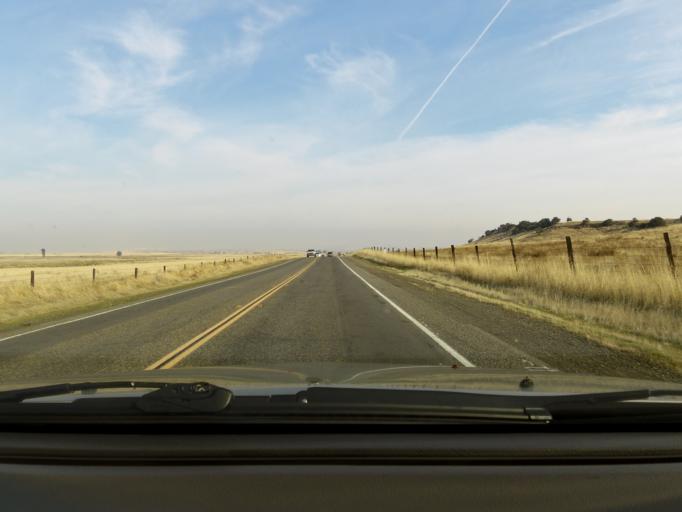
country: US
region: California
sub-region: Madera County
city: Bonadelle Ranchos-Madera Ranchos
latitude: 36.9828
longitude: -119.7940
